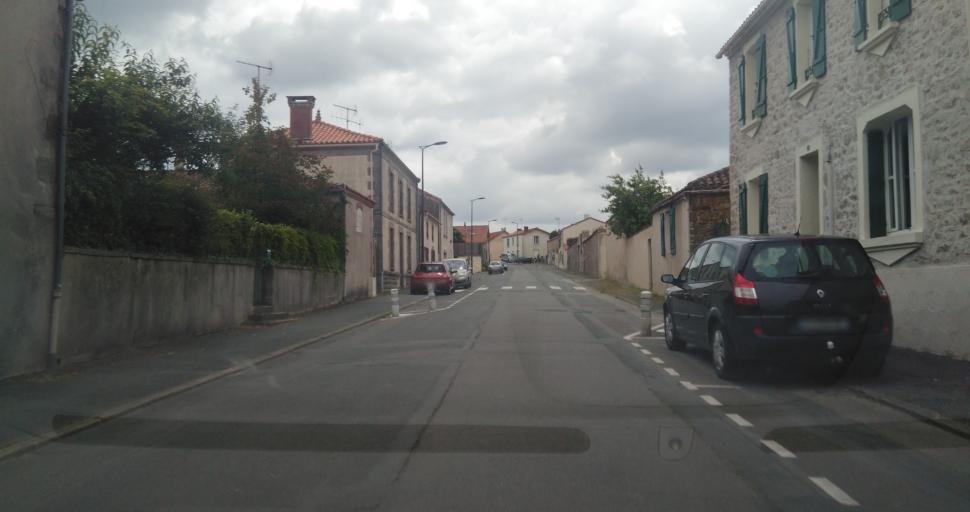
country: FR
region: Pays de la Loire
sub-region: Departement de la Vendee
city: La Chaize-le-Vicomte
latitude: 46.6704
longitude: -1.2905
